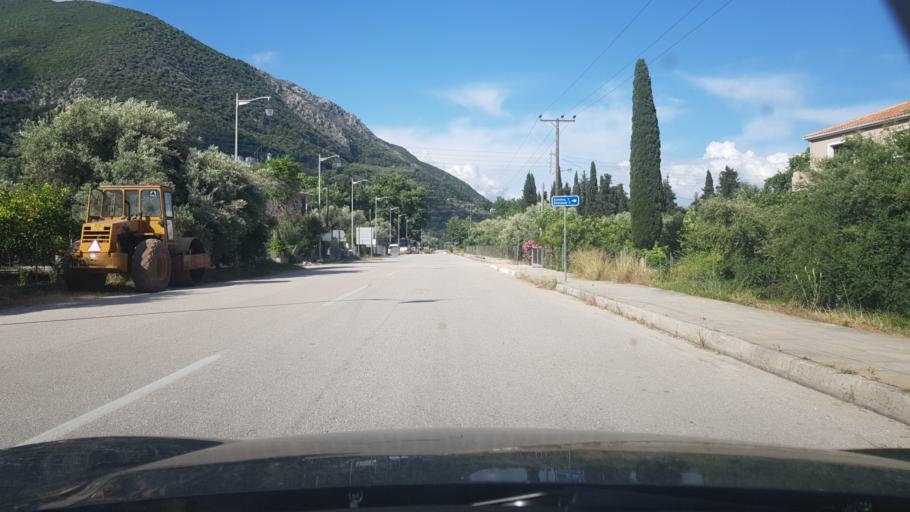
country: GR
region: Ionian Islands
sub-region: Lefkada
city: Nidri
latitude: 38.7108
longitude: 20.7067
